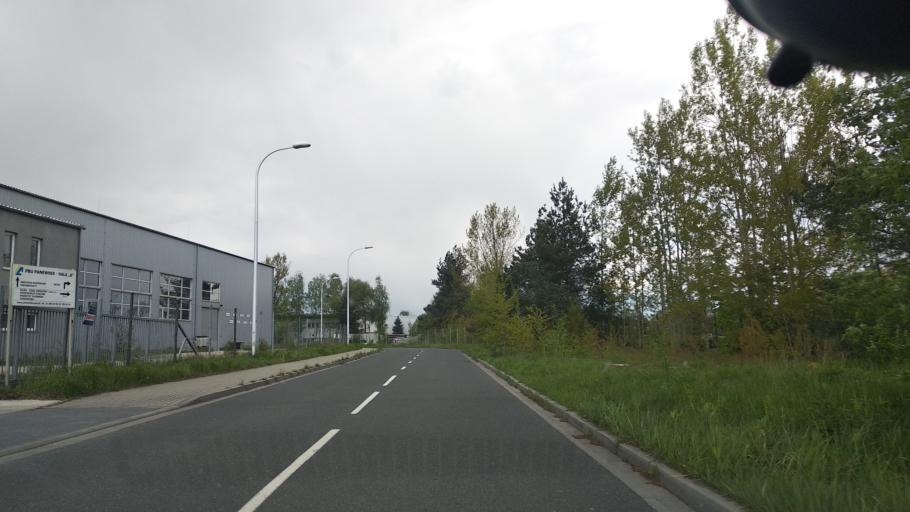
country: PL
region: Silesian Voivodeship
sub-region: Powiat mikolowski
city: Mikolow
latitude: 50.2223
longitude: 18.9238
